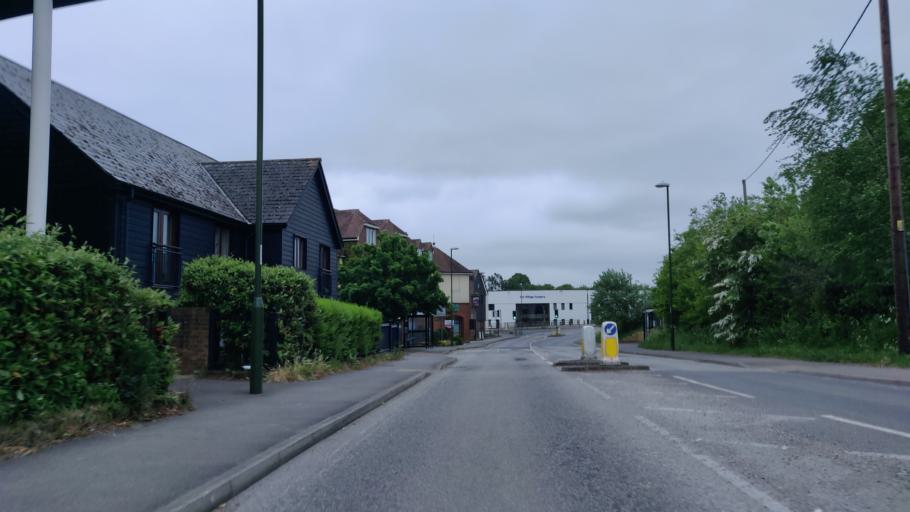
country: GB
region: England
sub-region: West Sussex
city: Southwater
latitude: 51.0254
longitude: -0.3522
